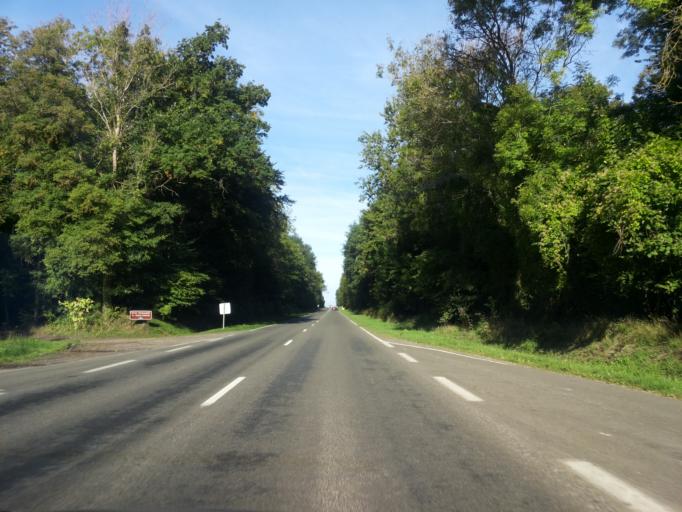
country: FR
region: Picardie
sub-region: Departement de l'Aisne
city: Crepy
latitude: 49.6227
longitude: 3.4471
